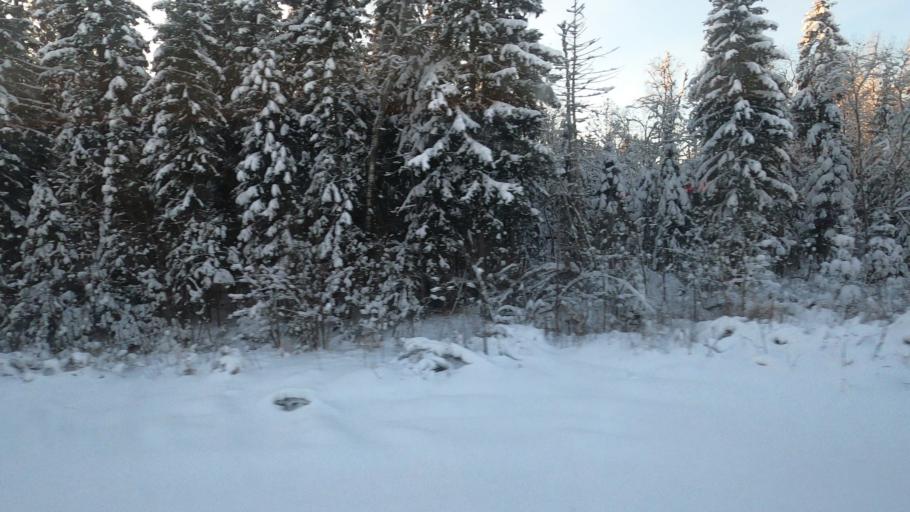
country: RU
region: Moskovskaya
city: Novo-Nikol'skoye
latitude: 56.6158
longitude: 37.5664
